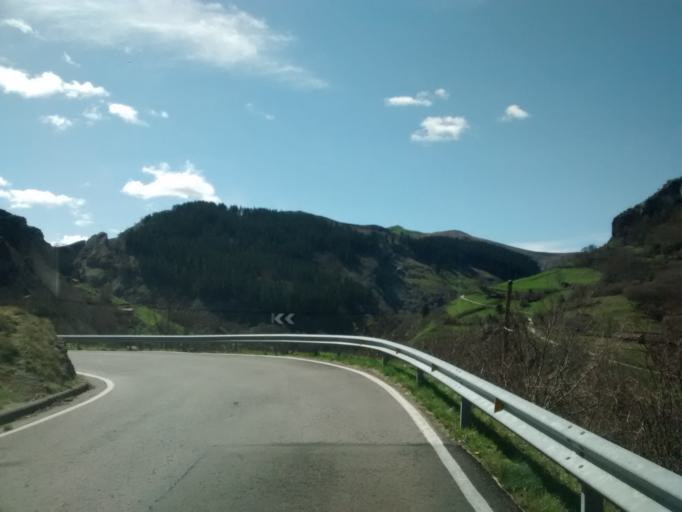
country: ES
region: Cantabria
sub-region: Provincia de Cantabria
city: Lierganes
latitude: 43.2644
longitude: -3.7127
